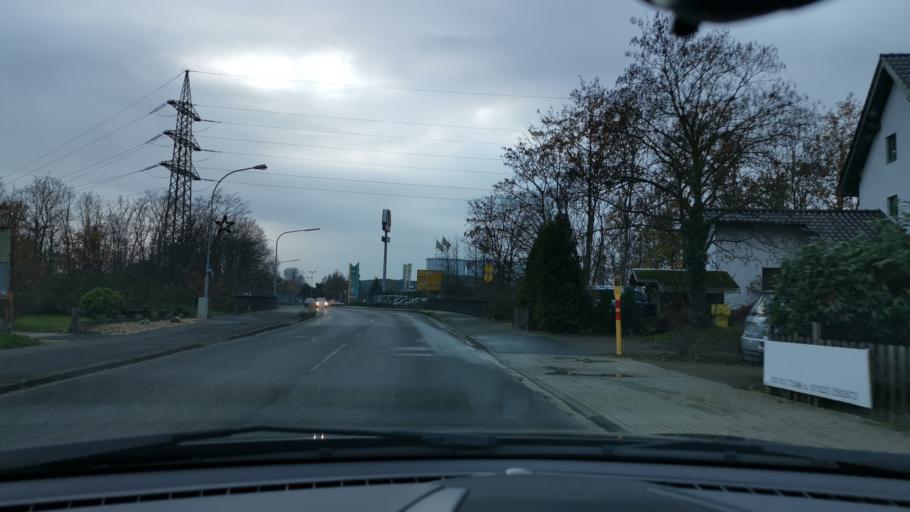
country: DE
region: North Rhine-Westphalia
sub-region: Regierungsbezirk Dusseldorf
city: Grevenbroich
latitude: 51.0968
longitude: 6.6094
